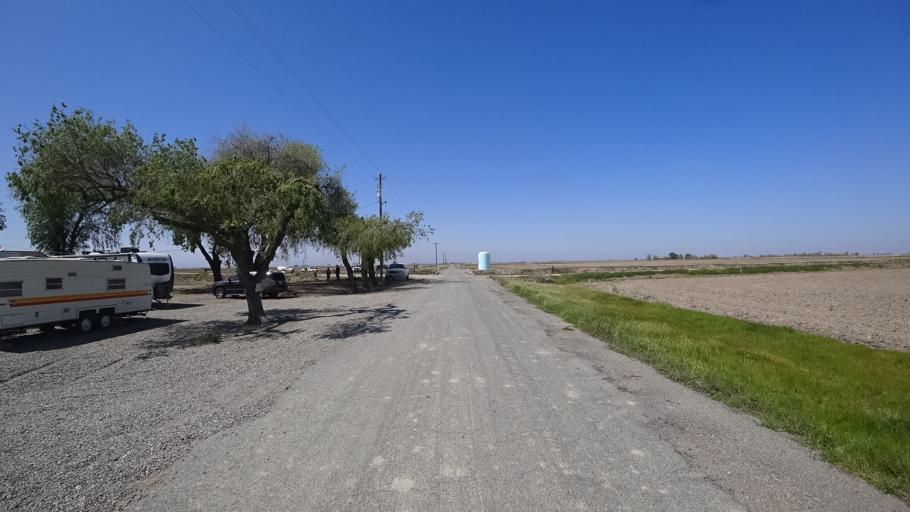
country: US
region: California
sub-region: Glenn County
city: Willows
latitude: 39.4929
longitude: -122.0833
